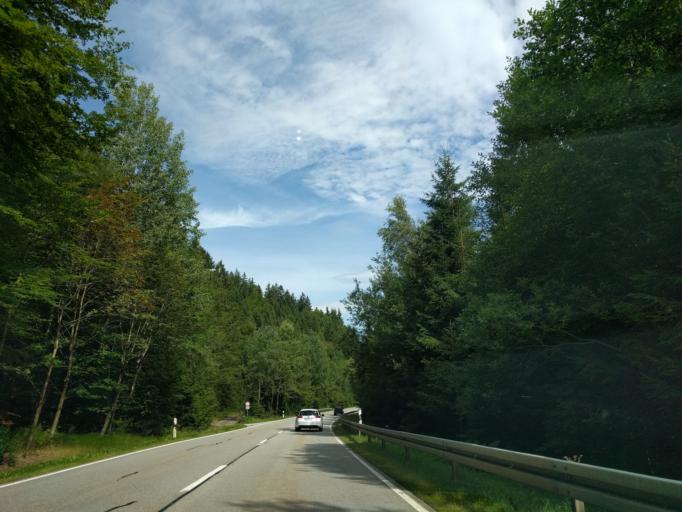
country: DE
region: Bavaria
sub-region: Lower Bavaria
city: Bodenmais
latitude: 49.0409
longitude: 13.1162
